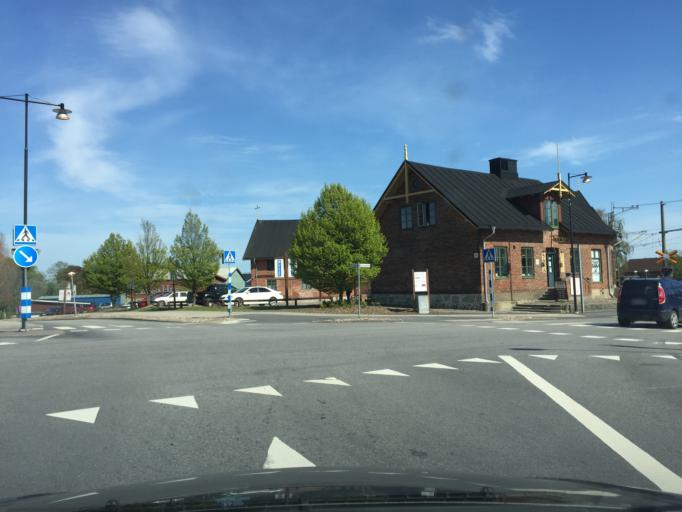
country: SE
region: Skane
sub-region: Skurups Kommun
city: Skurup
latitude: 55.4799
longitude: 13.5020
